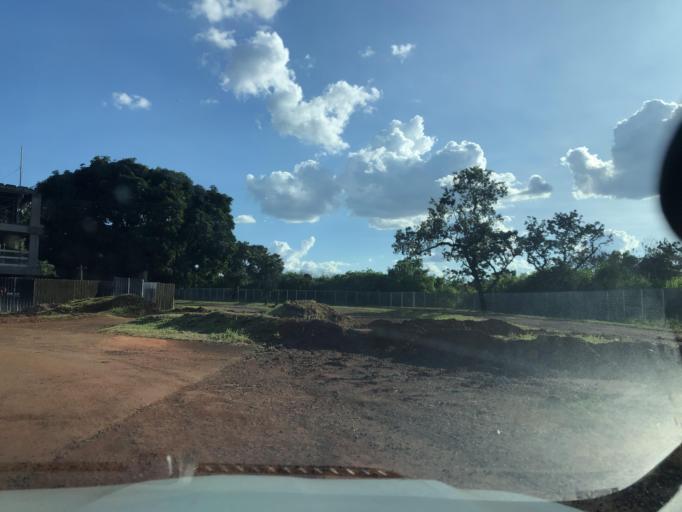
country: BR
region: Federal District
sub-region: Brasilia
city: Brasilia
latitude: -15.7429
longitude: -47.9042
